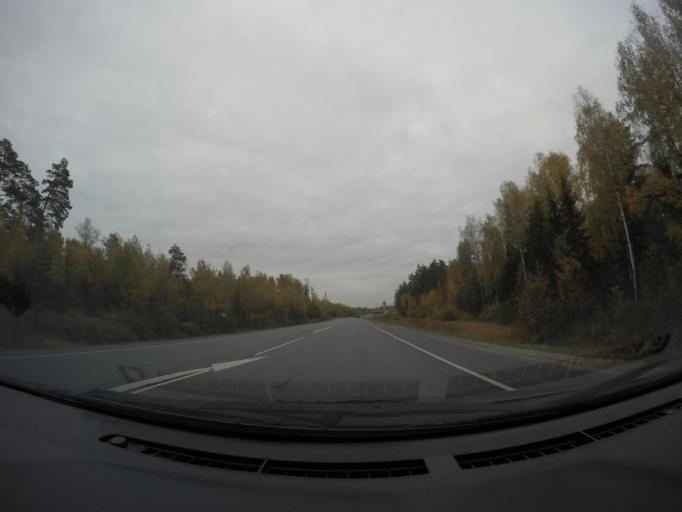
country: RU
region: Moskovskaya
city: Fryazevo
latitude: 55.7033
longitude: 38.4331
